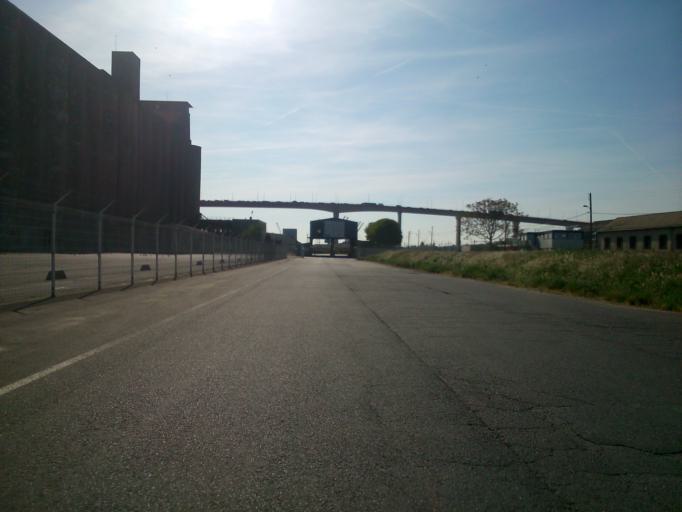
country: FR
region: Pays de la Loire
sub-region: Departement de la Loire-Atlantique
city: Bouguenais
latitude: 47.1947
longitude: -1.6058
